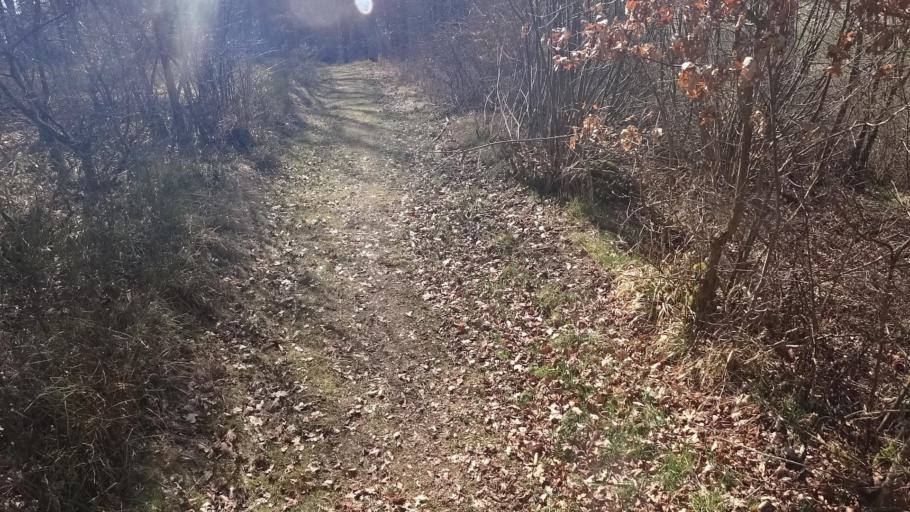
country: DE
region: Rheinland-Pfalz
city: Rheinbollen
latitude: 50.0179
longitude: 7.6769
